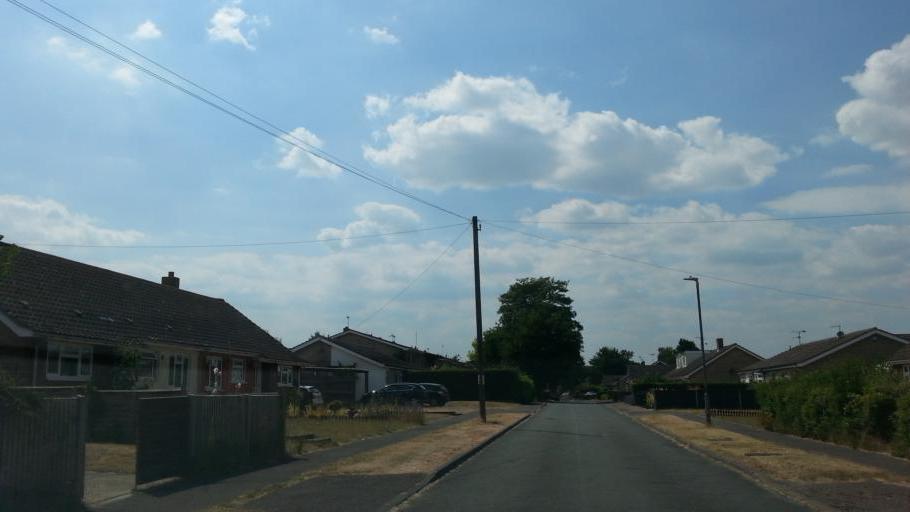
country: GB
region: England
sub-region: Cambridgeshire
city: Isleham
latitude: 52.3037
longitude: 0.4945
